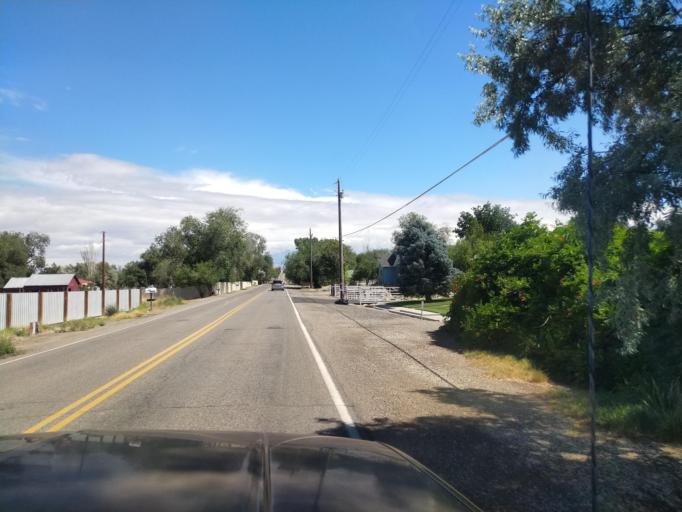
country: US
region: Colorado
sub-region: Mesa County
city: Redlands
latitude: 39.1220
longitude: -108.6081
